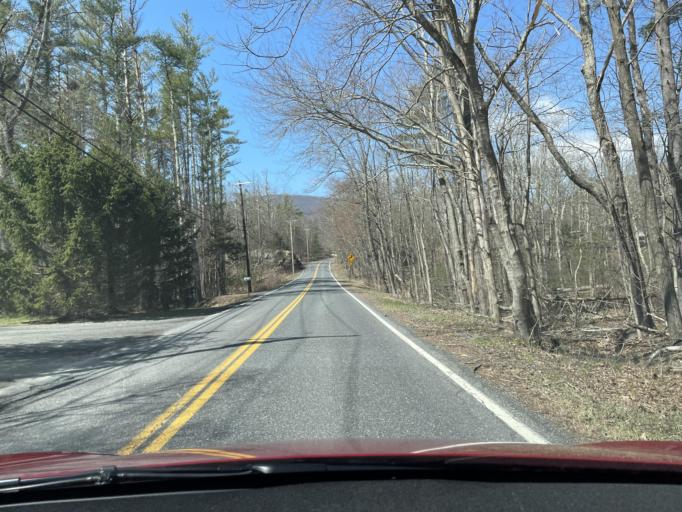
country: US
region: New York
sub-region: Ulster County
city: Manorville
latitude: 42.1057
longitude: -74.0243
